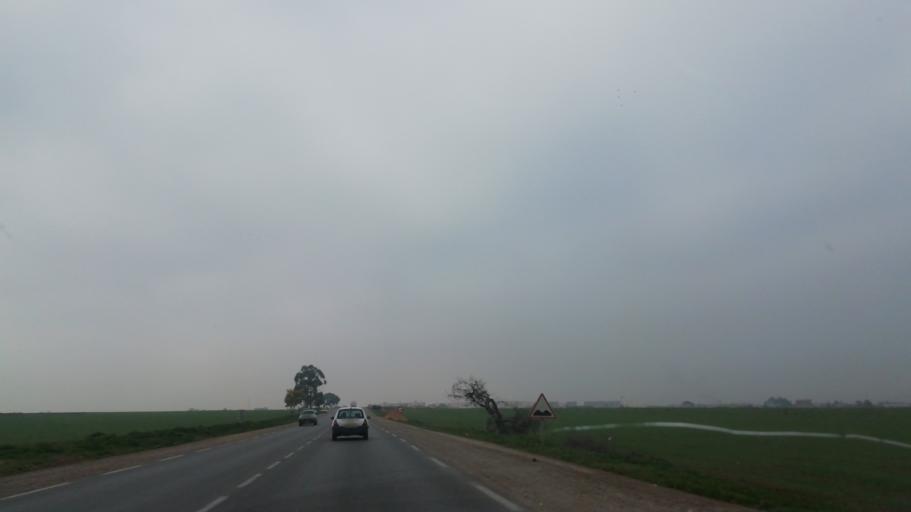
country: DZ
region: Relizane
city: Djidiouia
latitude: 35.8962
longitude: 0.7495
